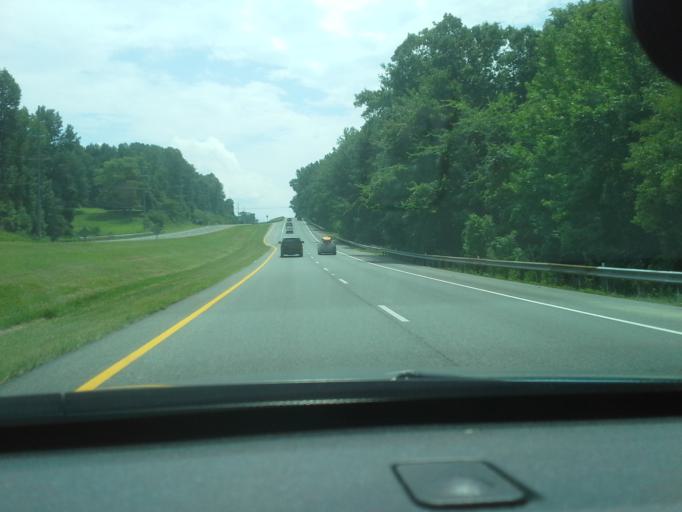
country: US
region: Maryland
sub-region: Calvert County
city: Dunkirk Town Center
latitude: 38.6989
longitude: -76.6446
